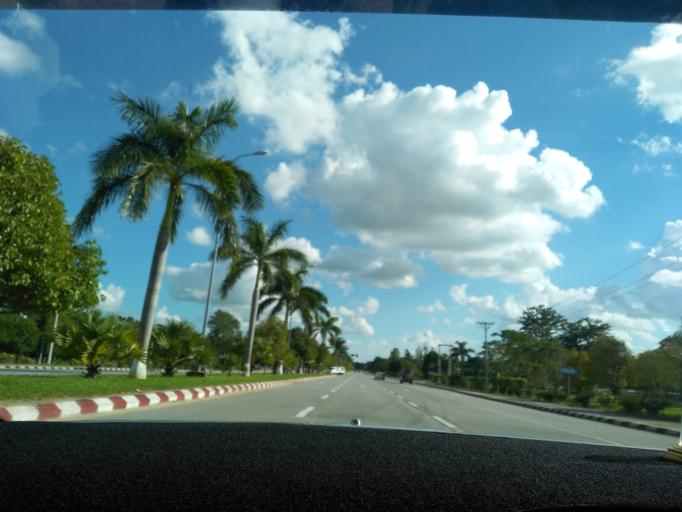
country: MM
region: Mandalay
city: Nay Pyi Taw
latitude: 19.7292
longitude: 96.1111
